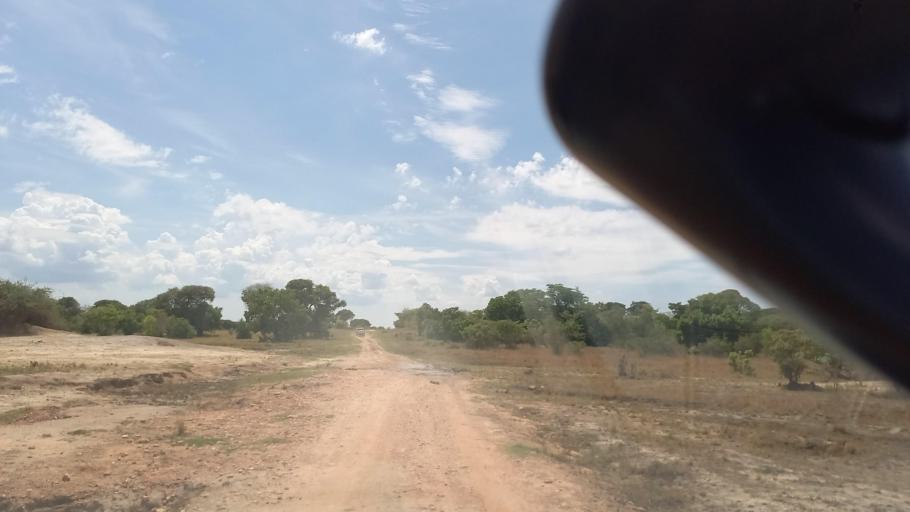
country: ZM
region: Southern
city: Mazabuka
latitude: -16.1393
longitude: 27.7603
